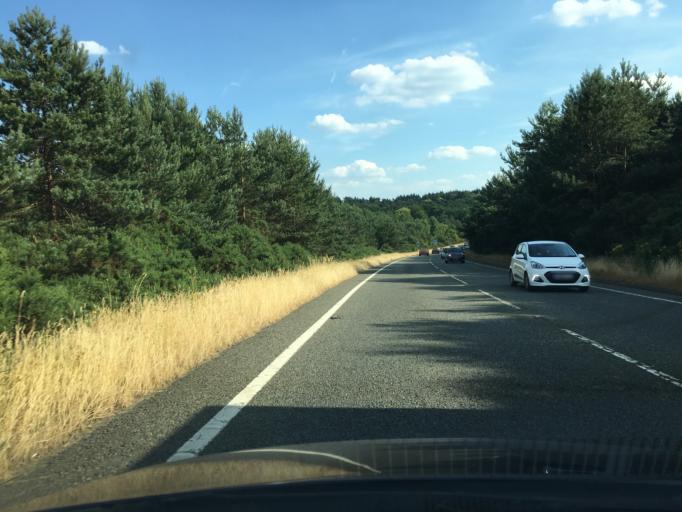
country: GB
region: England
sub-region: Bracknell Forest
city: Crowthorne
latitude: 51.3720
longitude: -0.7656
